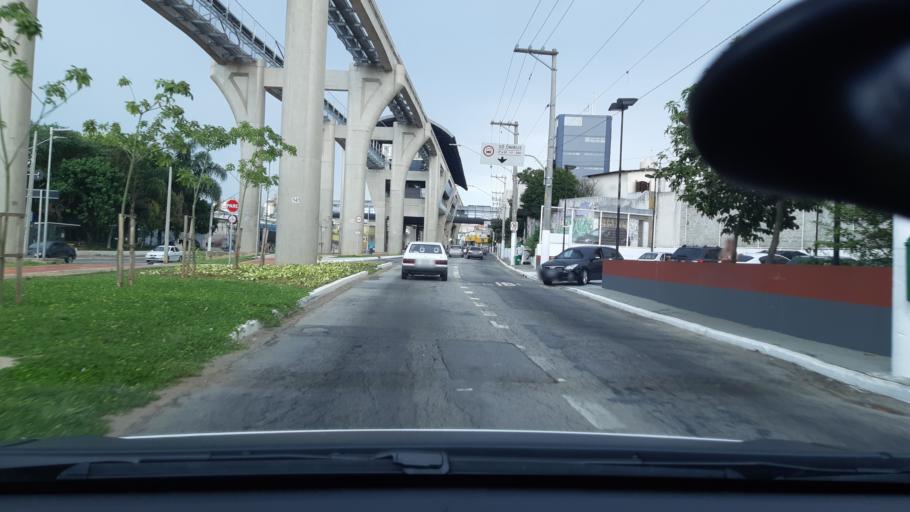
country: BR
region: Sao Paulo
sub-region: Sao Caetano Do Sul
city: Sao Caetano do Sul
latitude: -23.6000
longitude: -46.5288
